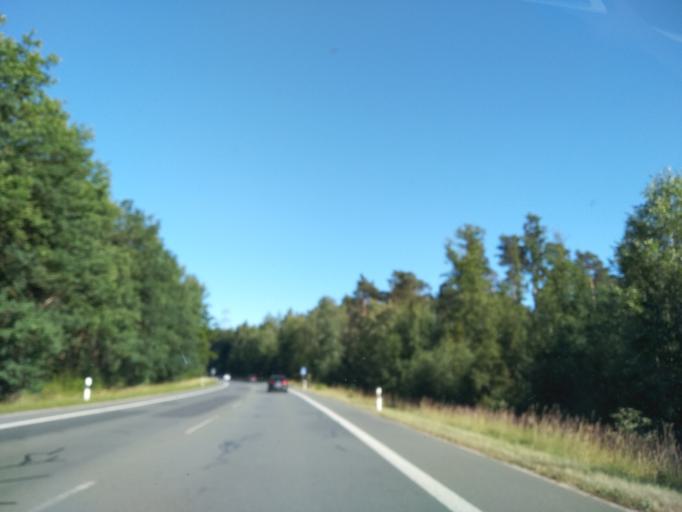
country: DE
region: Bavaria
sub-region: Regierungsbezirk Mittelfranken
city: Hessdorf
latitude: 49.6184
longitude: 10.9534
